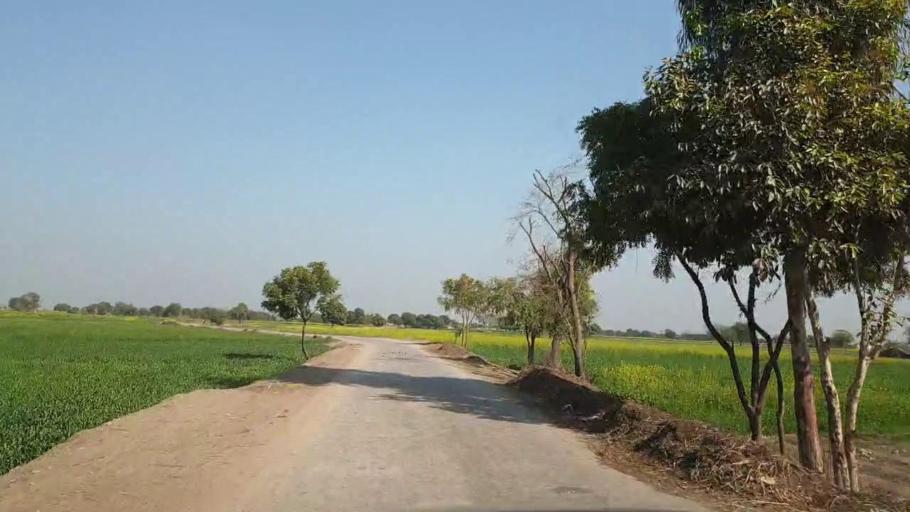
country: PK
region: Sindh
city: Tando Allahyar
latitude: 25.5704
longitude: 68.7160
